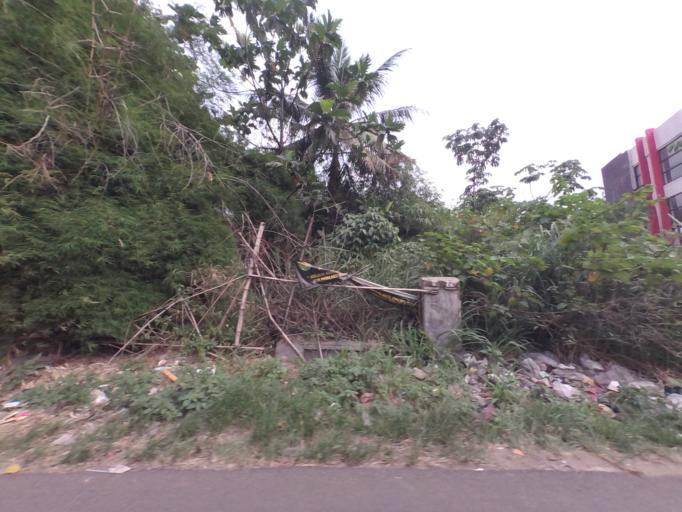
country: ID
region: West Java
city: Ciampea
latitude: -6.5586
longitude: 106.6921
